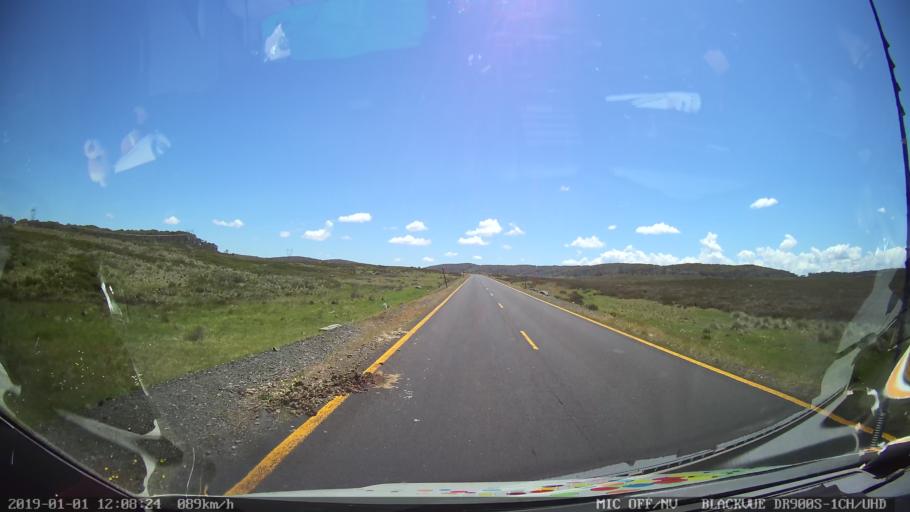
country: AU
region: New South Wales
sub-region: Tumut Shire
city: Tumut
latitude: -35.8208
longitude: 148.4945
